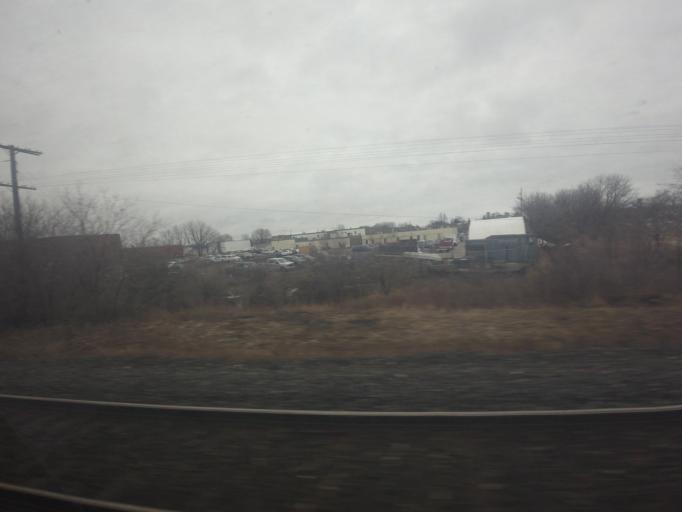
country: CA
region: Ontario
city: Kingston
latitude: 44.2392
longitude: -76.5739
